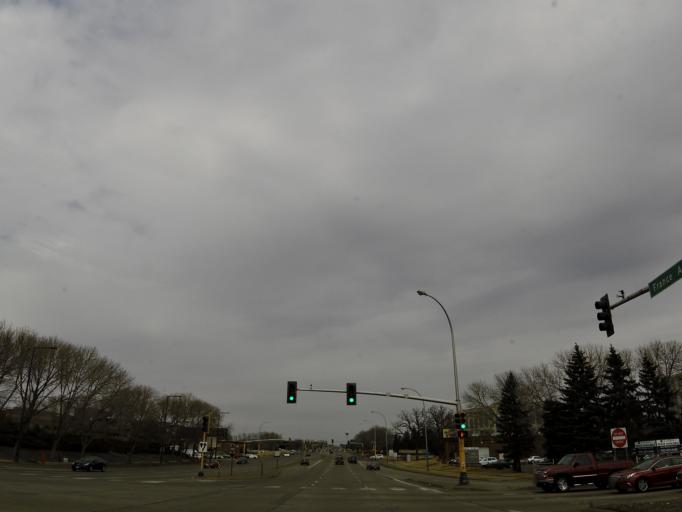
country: US
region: Minnesota
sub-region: Hennepin County
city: Bloomington
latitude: 44.8603
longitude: -93.3287
